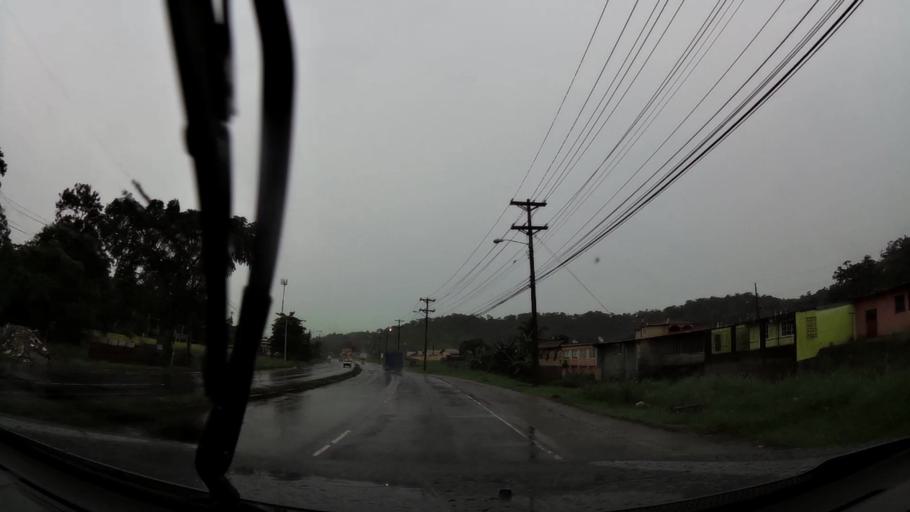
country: PA
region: Colon
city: Sabanitas
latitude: 9.3574
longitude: -79.8168
